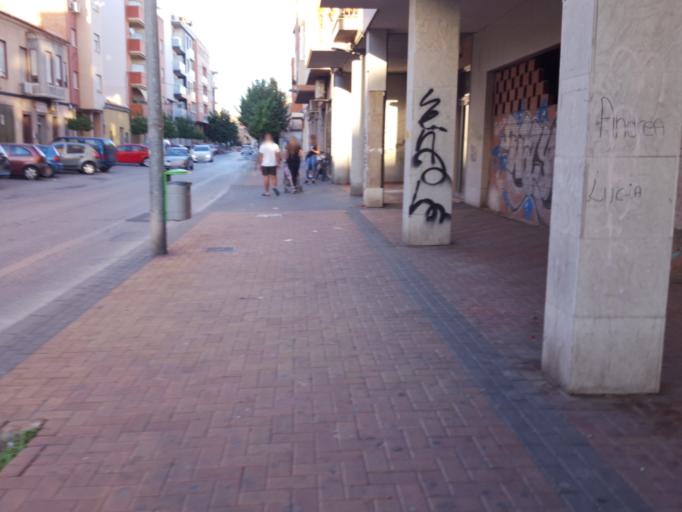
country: ES
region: Murcia
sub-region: Murcia
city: Murcia
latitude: 38.0083
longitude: -1.1581
